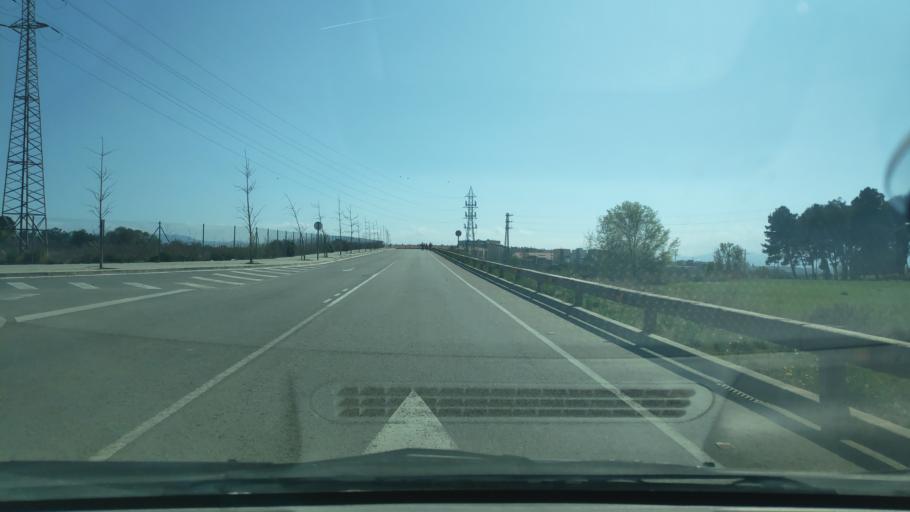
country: ES
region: Catalonia
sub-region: Provincia de Barcelona
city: Sabadell
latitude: 41.5557
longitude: 2.1220
